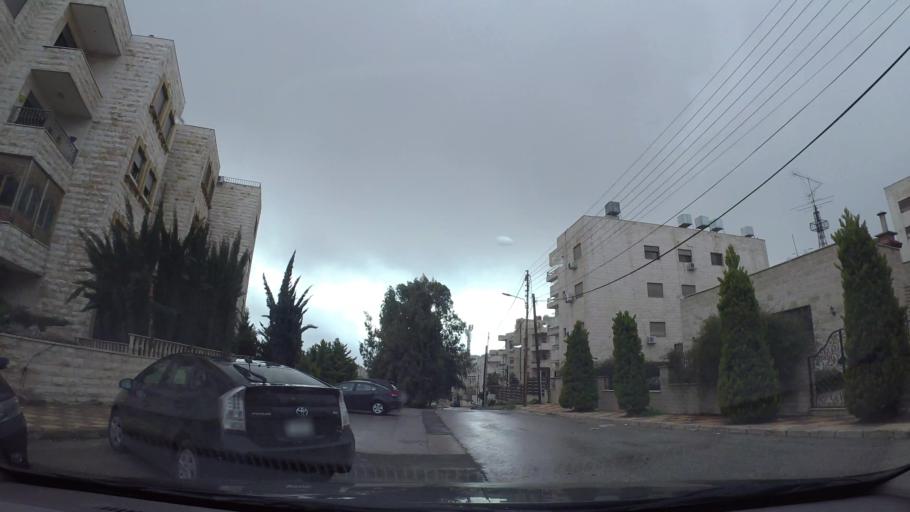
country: JO
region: Amman
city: Wadi as Sir
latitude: 31.9439
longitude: 35.8527
